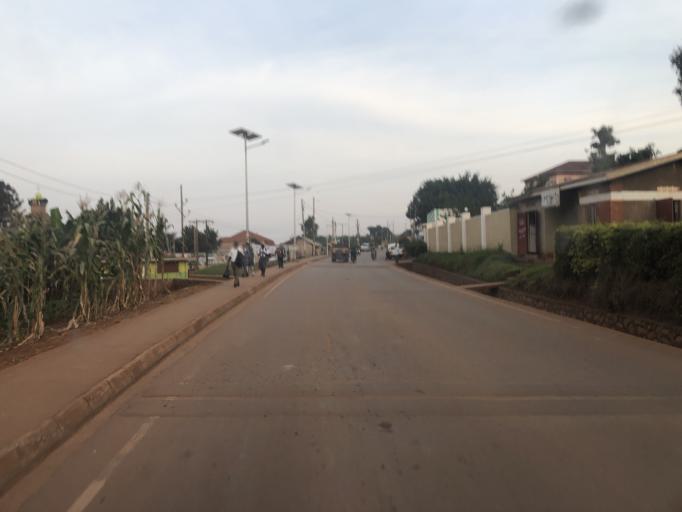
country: UG
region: Central Region
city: Kampala Central Division
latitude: 0.2903
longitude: 32.5359
